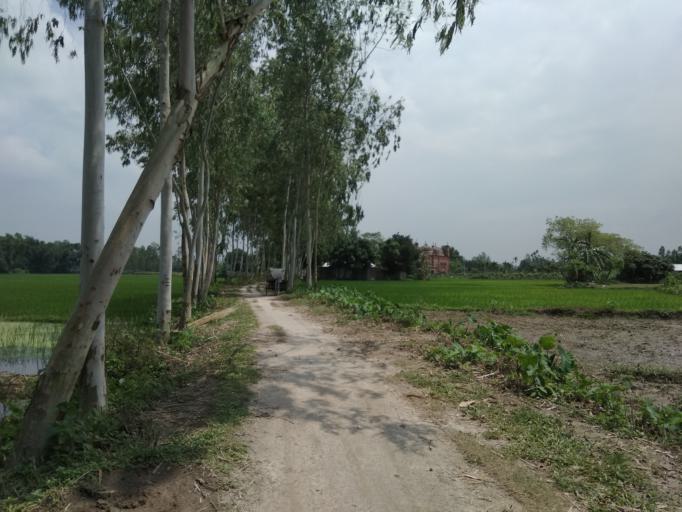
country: BD
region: Rangpur Division
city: Thakurgaon
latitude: 26.1265
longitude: 88.5626
